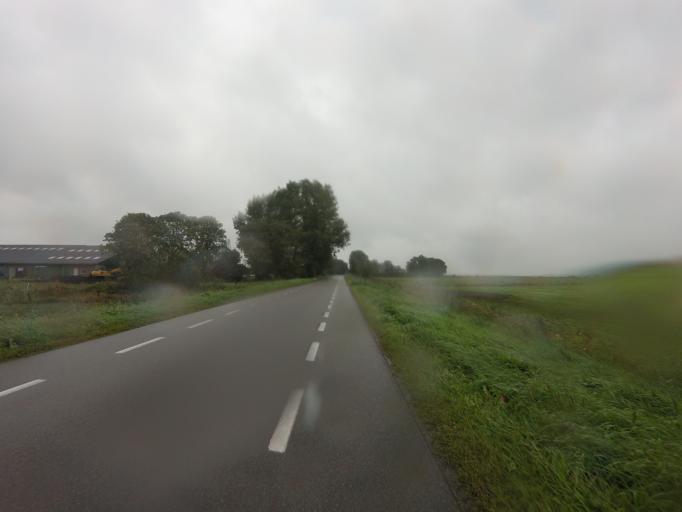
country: NL
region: Friesland
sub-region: Gemeente Smallingerland
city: Oudega
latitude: 53.0964
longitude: 5.9649
